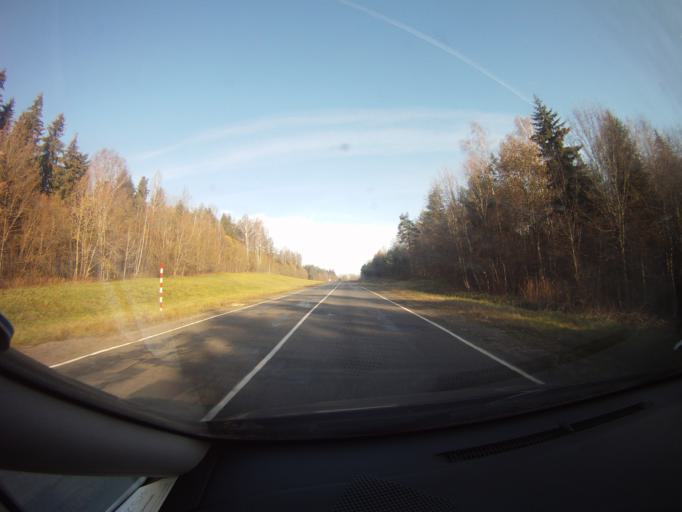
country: BY
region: Minsk
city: Syomkava
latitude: 54.2429
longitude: 27.4853
